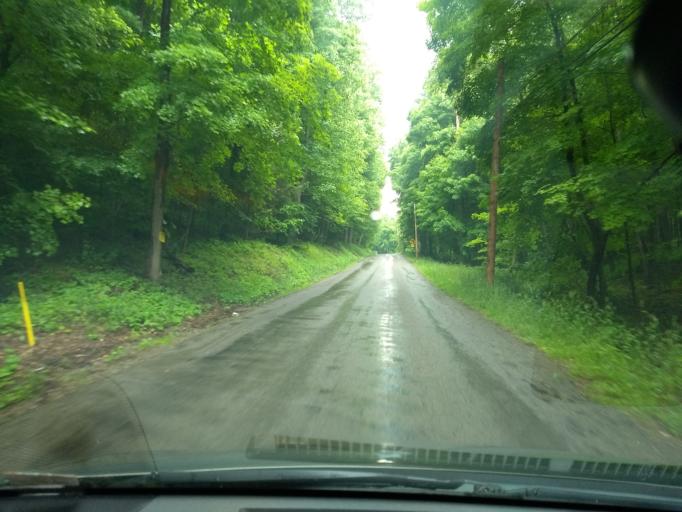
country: US
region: Pennsylvania
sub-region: Westmoreland County
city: Avonmore
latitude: 40.5300
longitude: -79.4915
